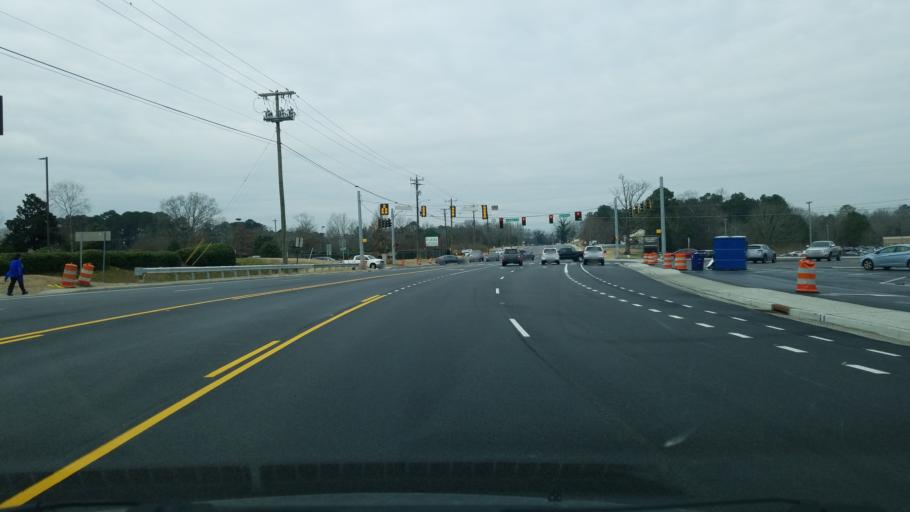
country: US
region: Tennessee
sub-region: Hamilton County
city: East Brainerd
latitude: 35.0008
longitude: -85.1315
